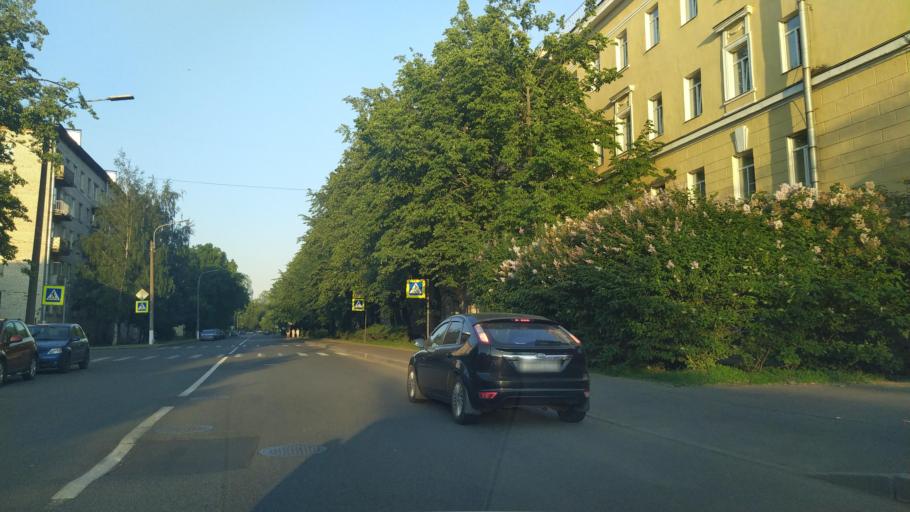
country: RU
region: St.-Petersburg
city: Kronshtadt
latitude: 59.9914
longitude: 29.7568
